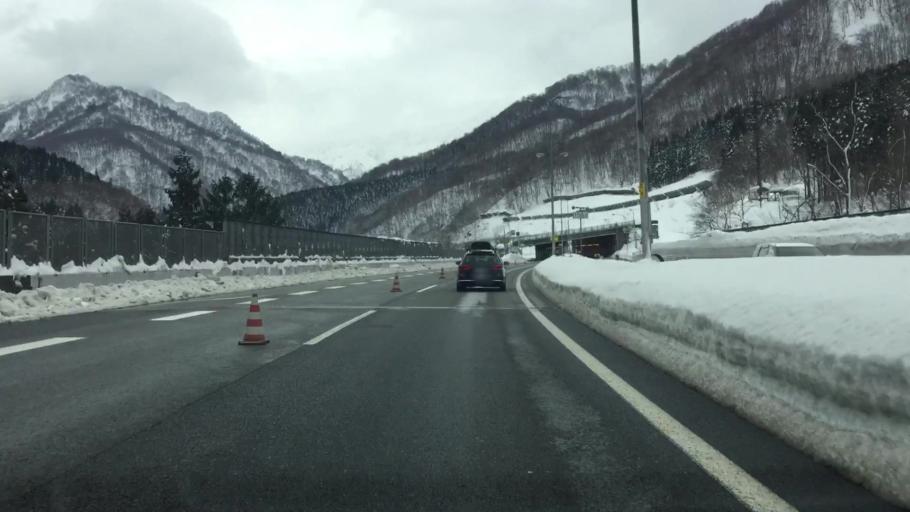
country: JP
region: Niigata
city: Shiozawa
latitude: 36.8735
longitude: 138.8641
